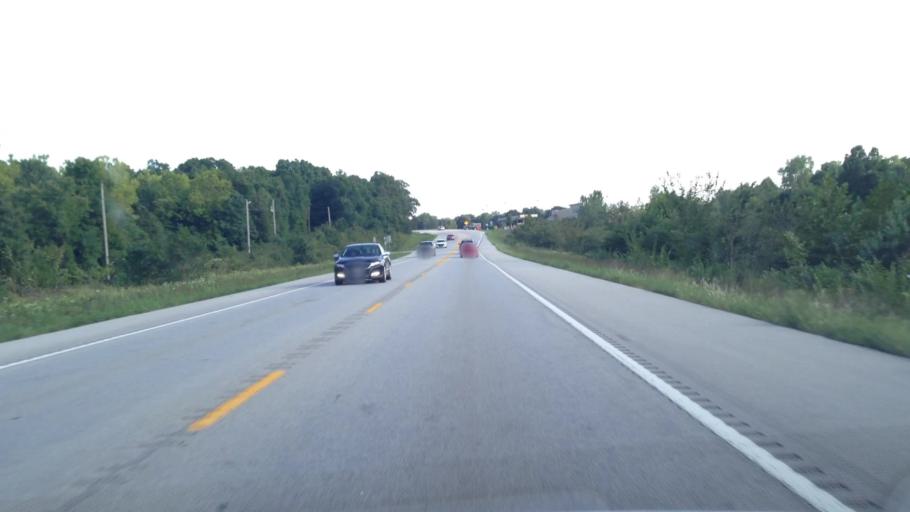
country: US
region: Missouri
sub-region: Jasper County
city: Carl Junction
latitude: 37.1488
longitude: -94.5243
